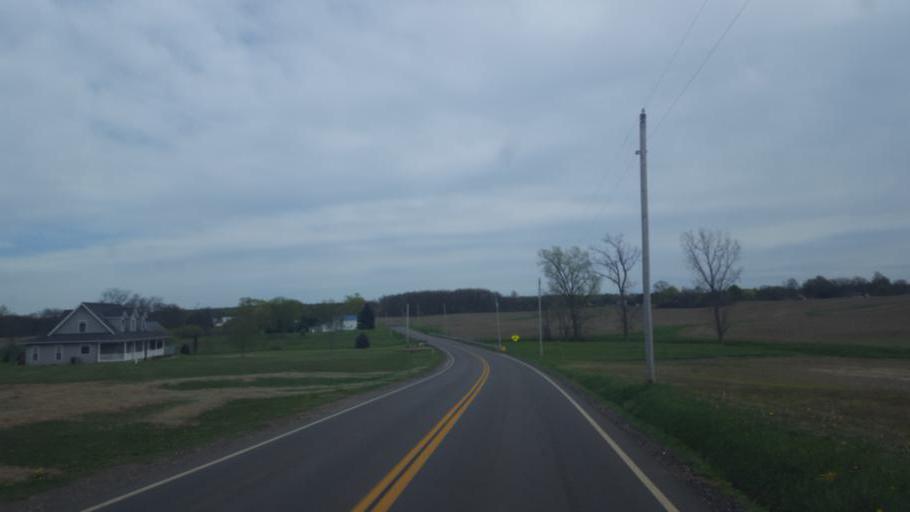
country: US
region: Ohio
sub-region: Crawford County
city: Galion
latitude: 40.7046
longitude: -82.7110
